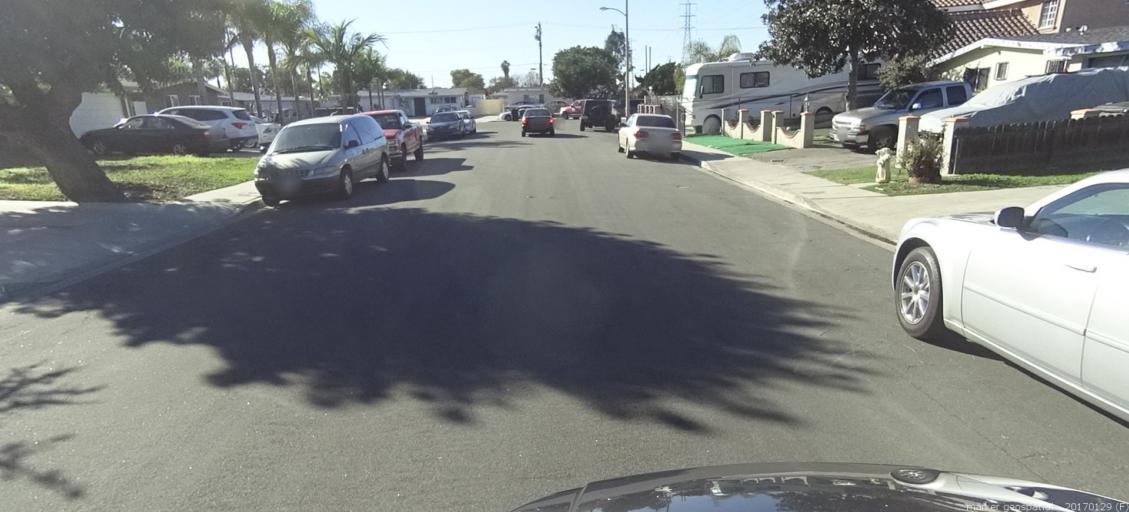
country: US
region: California
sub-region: Orange County
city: Stanton
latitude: 33.8063
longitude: -117.9662
